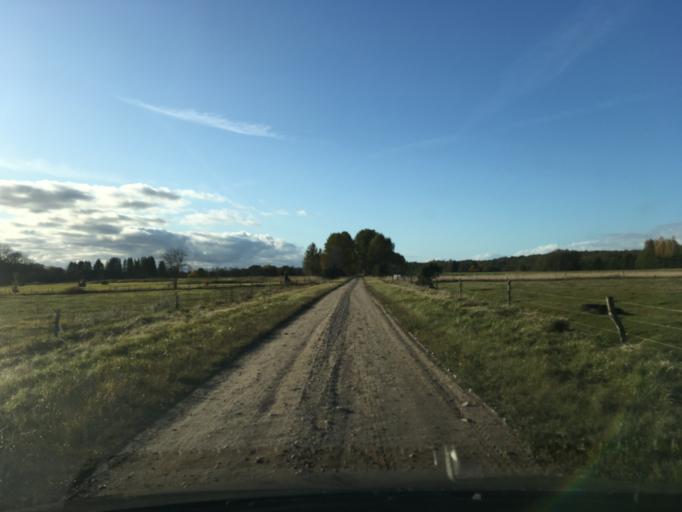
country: EE
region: Laeaene
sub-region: Lihula vald
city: Lihula
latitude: 58.5637
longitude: 23.8000
